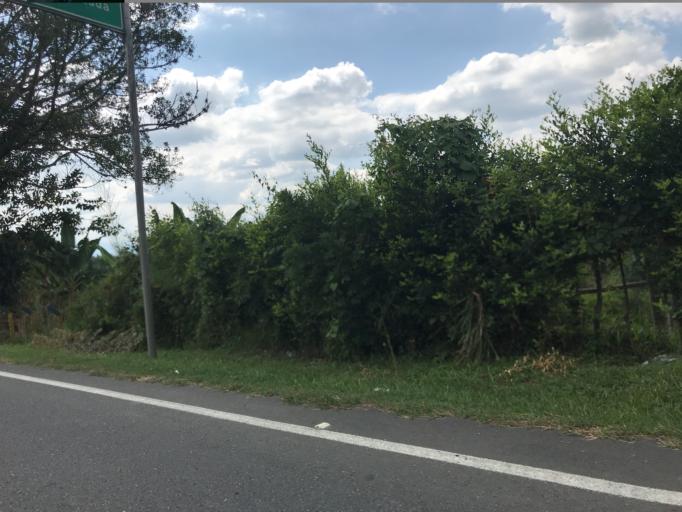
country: CO
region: Quindio
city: Armenia
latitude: 4.4844
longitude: -75.6974
